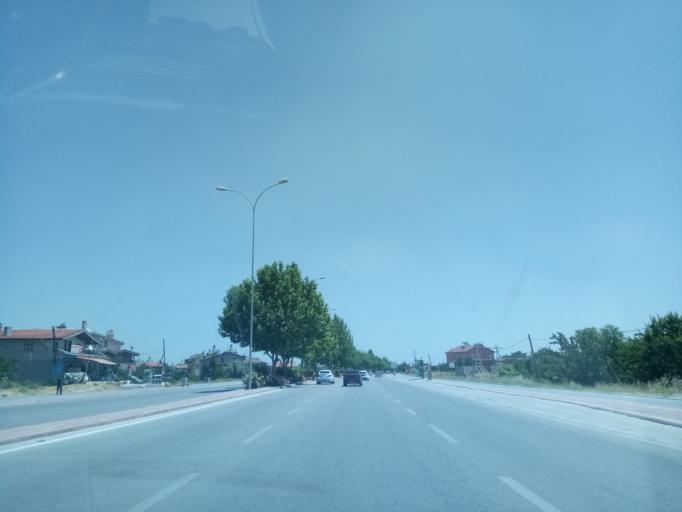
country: TR
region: Konya
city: Meram
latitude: 37.8243
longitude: 32.4659
